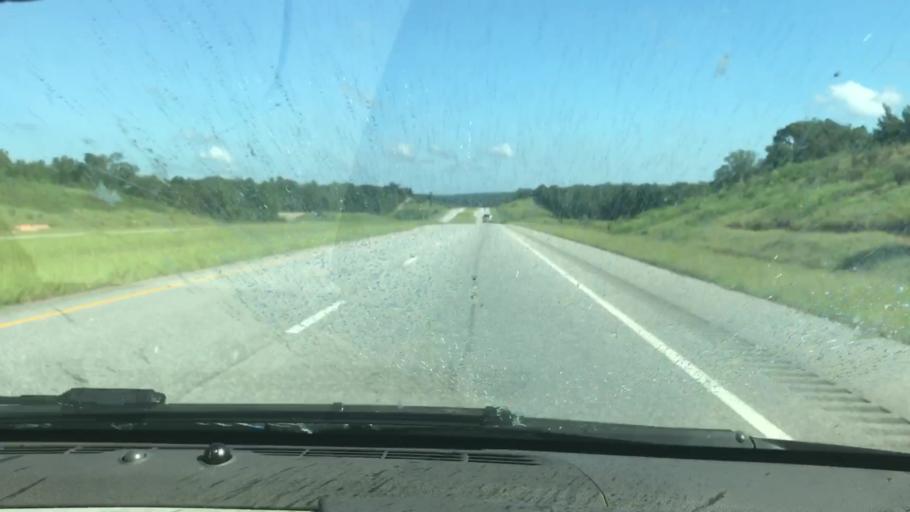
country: US
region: Alabama
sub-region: Barbour County
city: Eufaula
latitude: 32.0976
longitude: -85.1498
